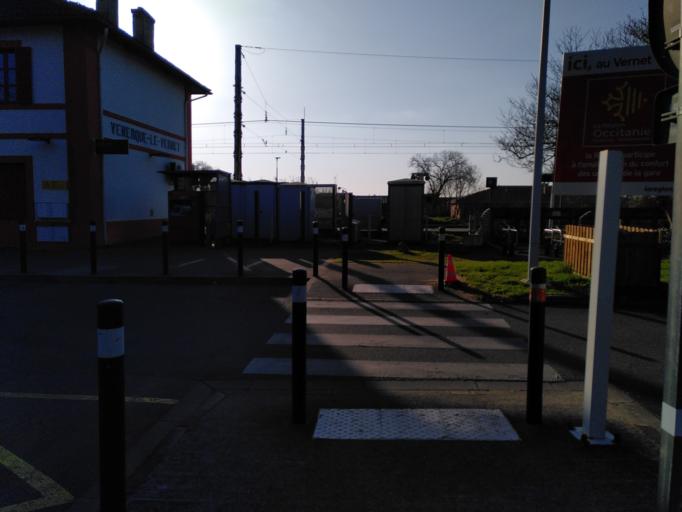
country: FR
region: Midi-Pyrenees
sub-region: Departement de la Haute-Garonne
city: Vernet
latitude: 43.4335
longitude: 1.4264
